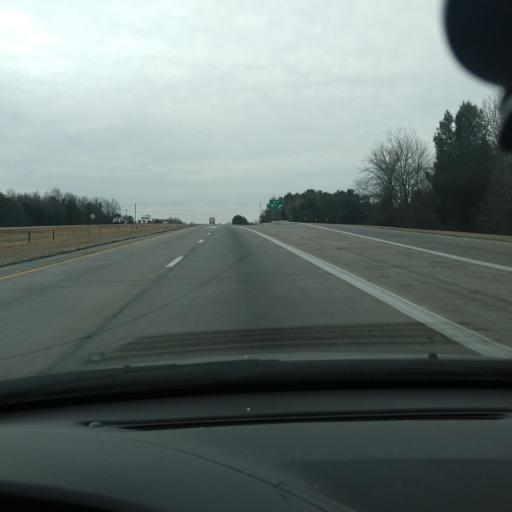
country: US
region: North Carolina
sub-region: Davidson County
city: Midway
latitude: 35.9419
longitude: -80.2353
